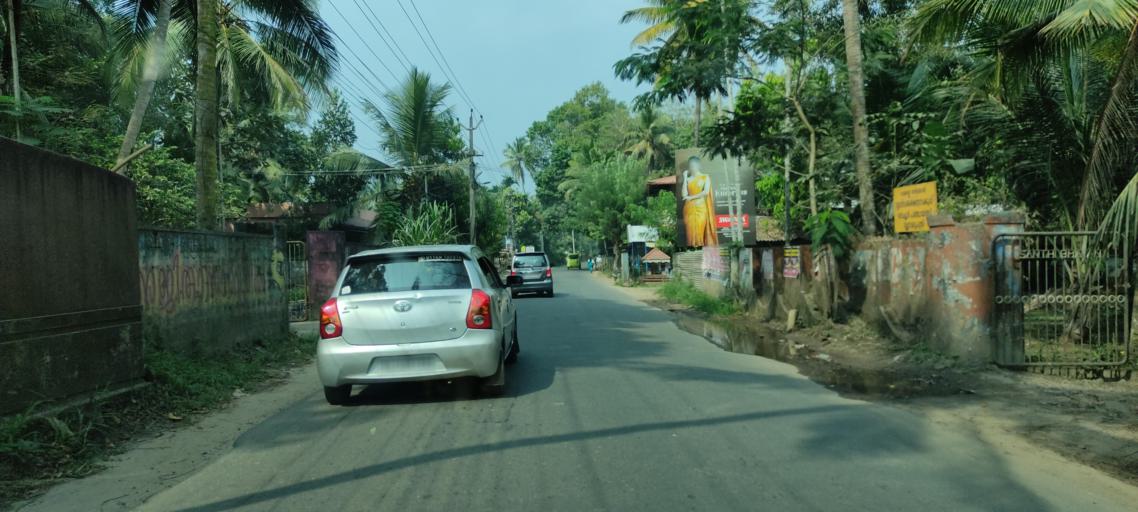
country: IN
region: Kerala
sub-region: Alappuzha
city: Shertallai
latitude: 9.6795
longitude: 76.4208
